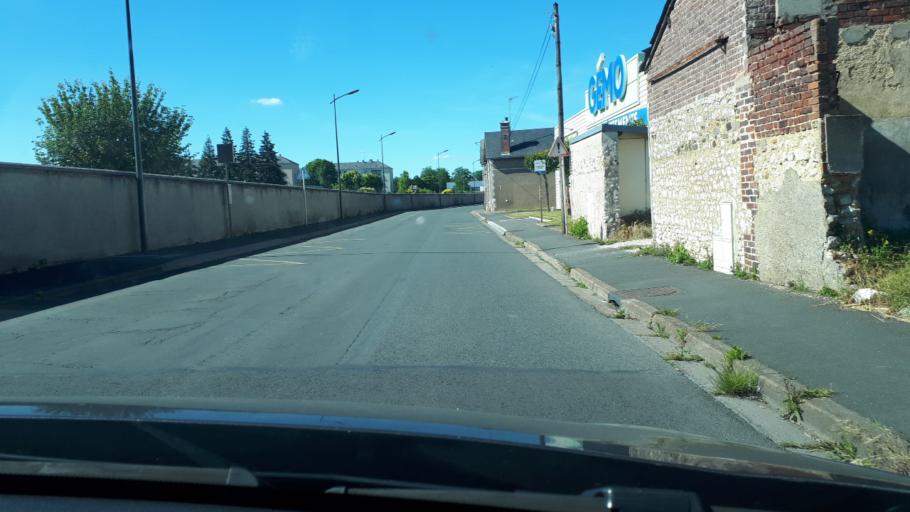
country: FR
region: Centre
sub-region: Departement du Loir-et-Cher
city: Vendome
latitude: 47.8042
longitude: 1.0700
